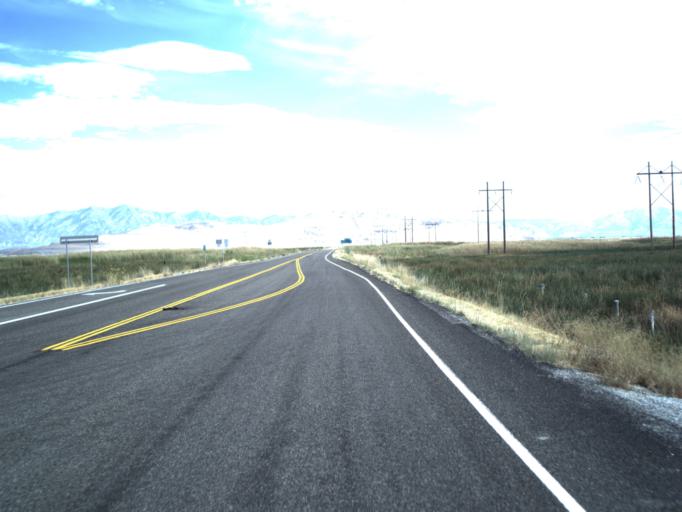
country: US
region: Utah
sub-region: Box Elder County
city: Tremonton
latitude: 41.6127
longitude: -112.3673
